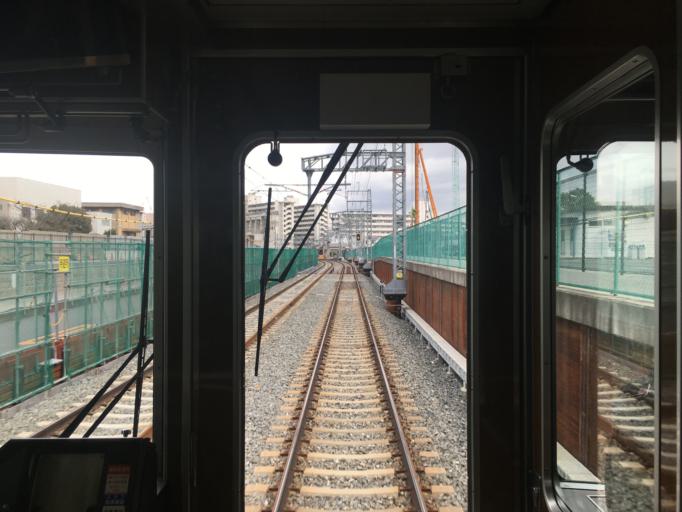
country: JP
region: Osaka
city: Suita
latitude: 34.7330
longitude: 135.5151
